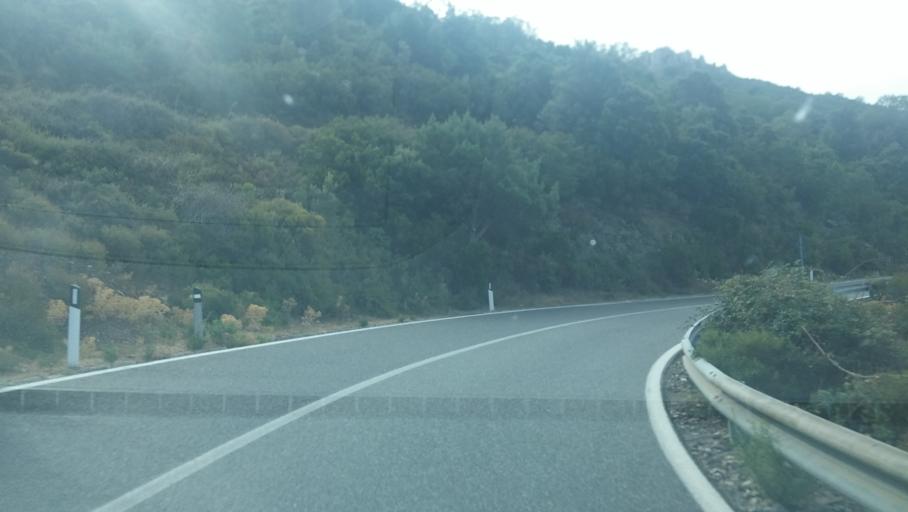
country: IT
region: Sardinia
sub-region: Provincia di Ogliastra
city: Urzulei
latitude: 40.1883
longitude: 9.5359
